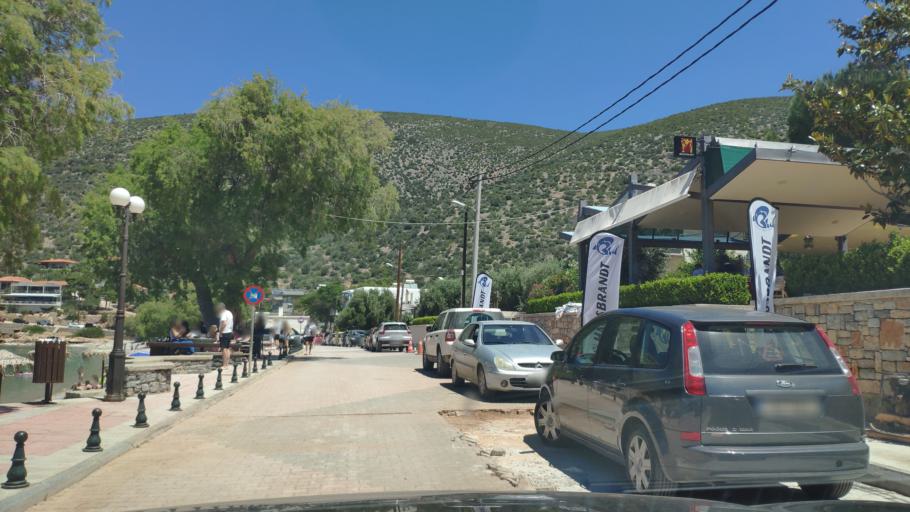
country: GR
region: Central Greece
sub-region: Nomos Voiotias
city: Kaparellion
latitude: 38.1817
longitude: 23.1431
